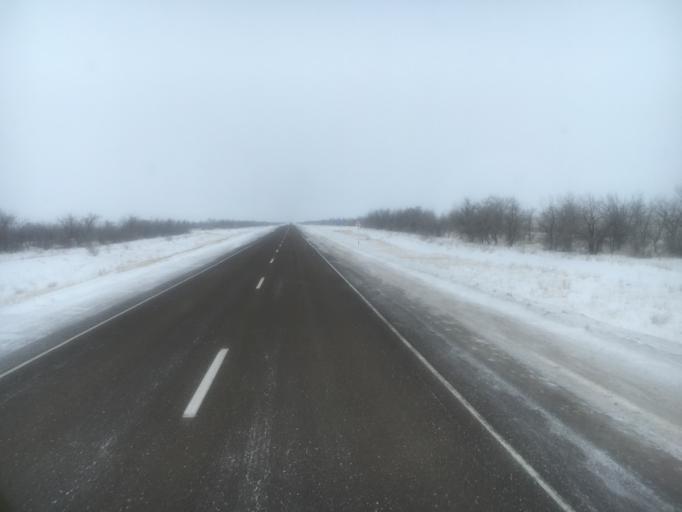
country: KZ
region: Aqtoebe
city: Martuk
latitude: 50.1557
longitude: 55.5474
